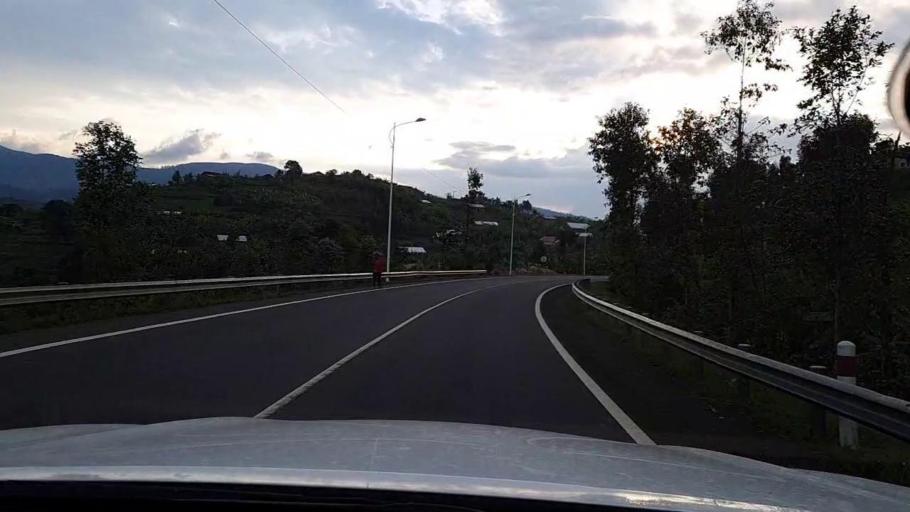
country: RW
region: Western Province
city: Kibuye
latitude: -2.0883
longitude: 29.4045
